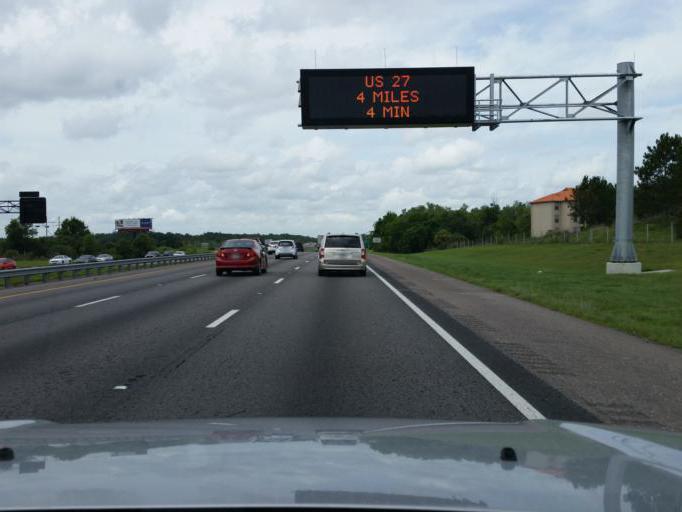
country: US
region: Florida
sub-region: Polk County
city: Loughman
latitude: 28.2692
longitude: -81.6056
